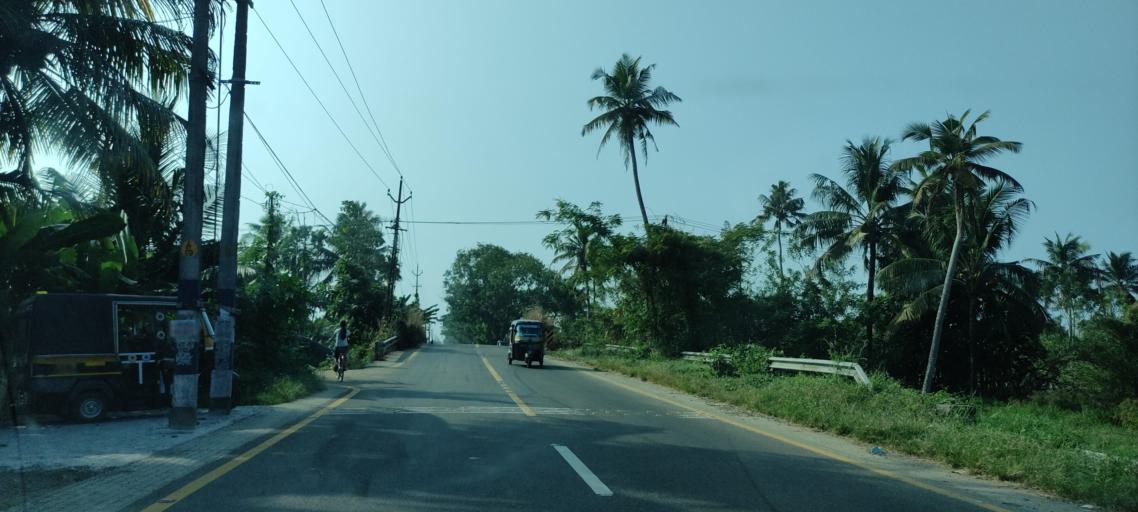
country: IN
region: Kerala
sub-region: Kottayam
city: Changanacheri
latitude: 9.3645
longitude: 76.4425
